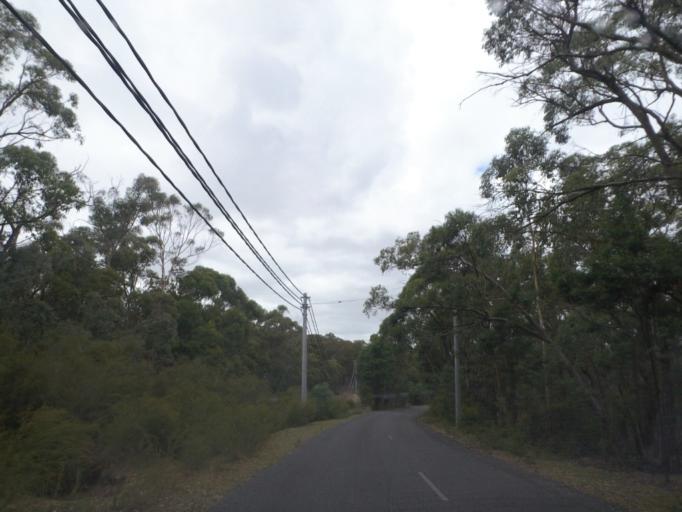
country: AU
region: Victoria
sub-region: Yarra Ranges
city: Chirnside Park
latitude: -37.6841
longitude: 145.3116
